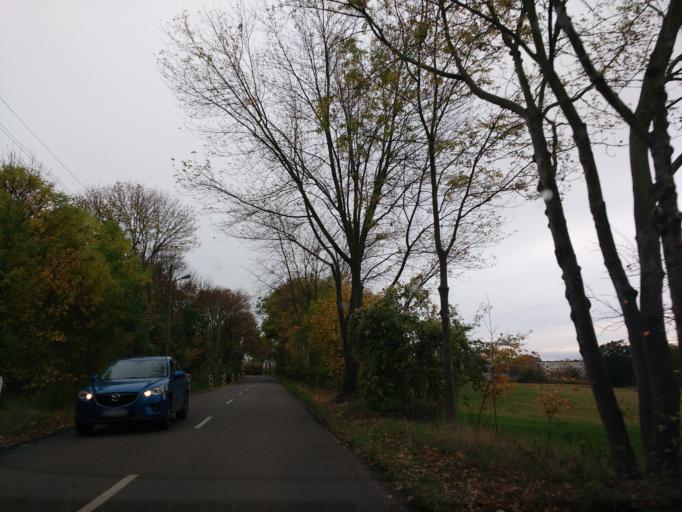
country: DE
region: Saxony-Anhalt
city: Gutenberg
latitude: 51.5225
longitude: 11.9675
